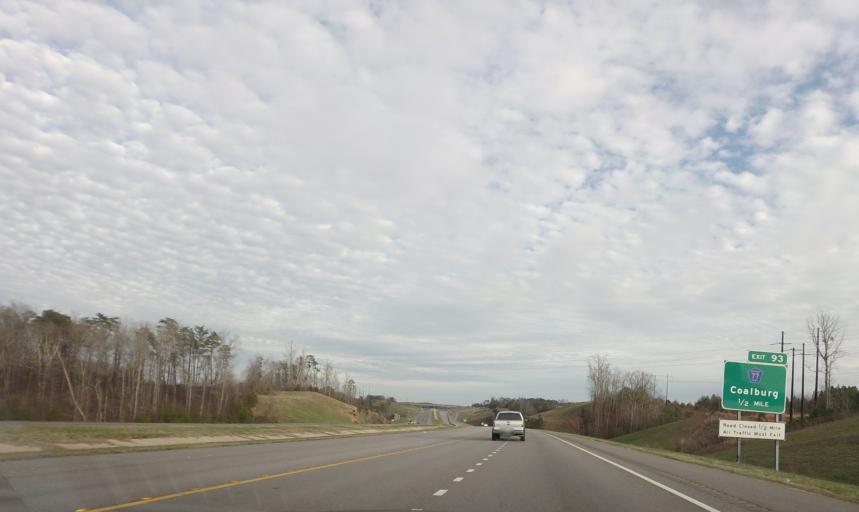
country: US
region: Alabama
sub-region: Jefferson County
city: Forestdale
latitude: 33.5897
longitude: -86.8703
